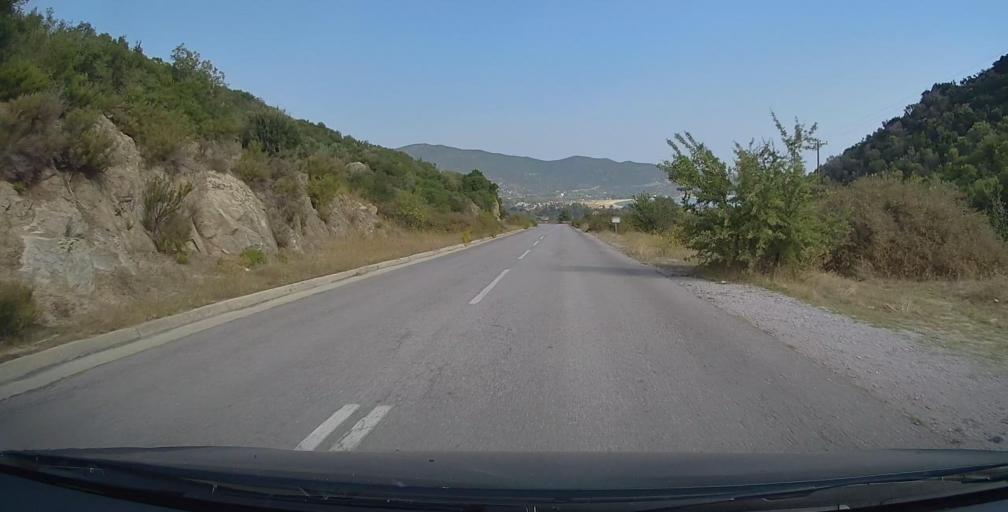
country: GR
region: Central Macedonia
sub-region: Nomos Chalkidikis
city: Sykia
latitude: 40.0262
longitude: 23.9882
